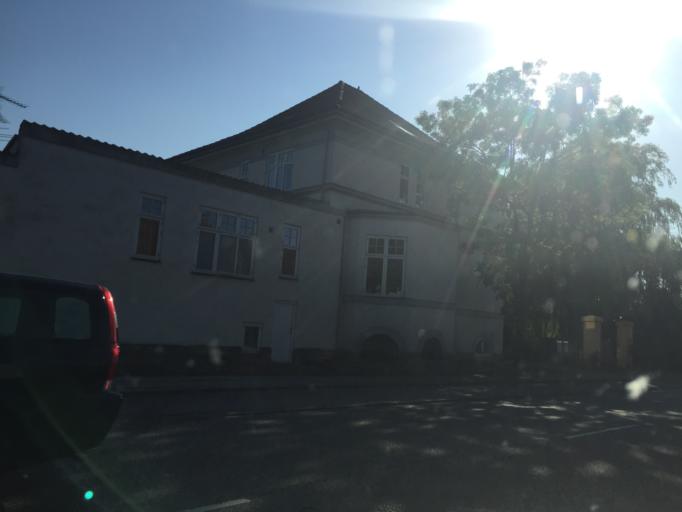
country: DK
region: Capital Region
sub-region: Lyngby-Tarbaek Kommune
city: Kongens Lyngby
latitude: 55.7618
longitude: 12.5392
